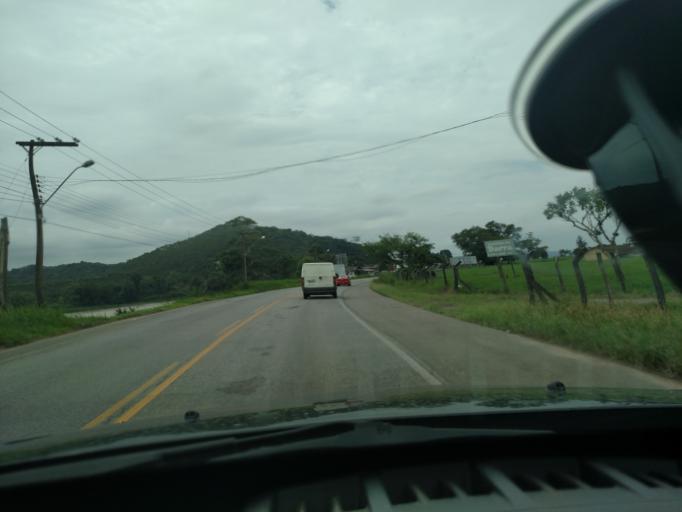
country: BR
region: Santa Catarina
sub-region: Itajai
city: Itajai
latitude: -26.8756
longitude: -48.7918
